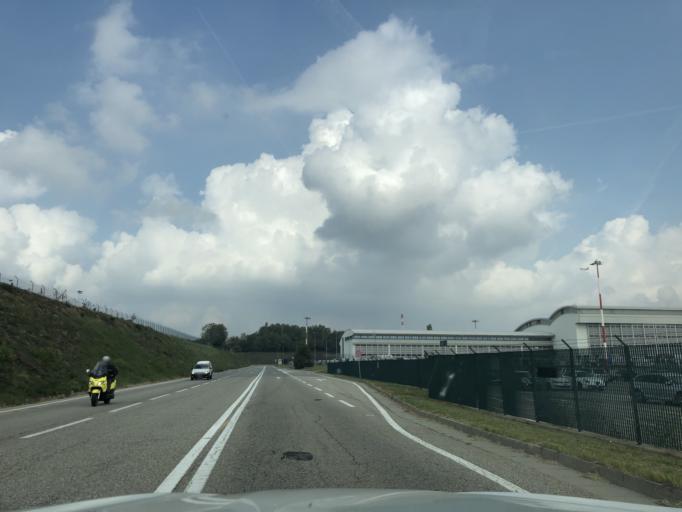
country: IT
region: Lombardy
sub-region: Provincia di Varese
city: Vizzola Ticino
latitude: 45.6322
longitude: 8.7087
